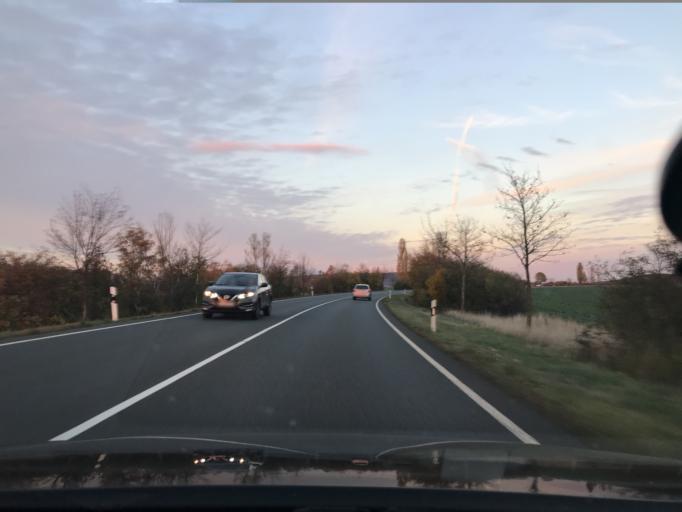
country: DE
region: Thuringia
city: Monchenholzhausen
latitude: 50.9705
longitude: 11.1689
